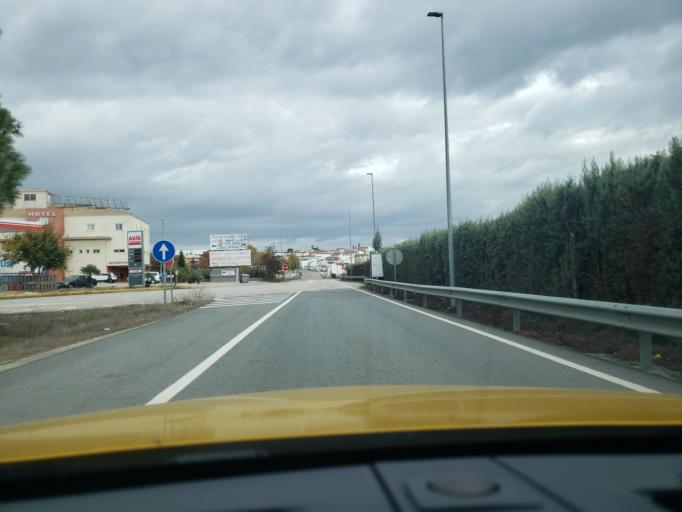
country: ES
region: Andalusia
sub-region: Provincia de Jaen
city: Guarroman
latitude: 38.1799
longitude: -3.6935
